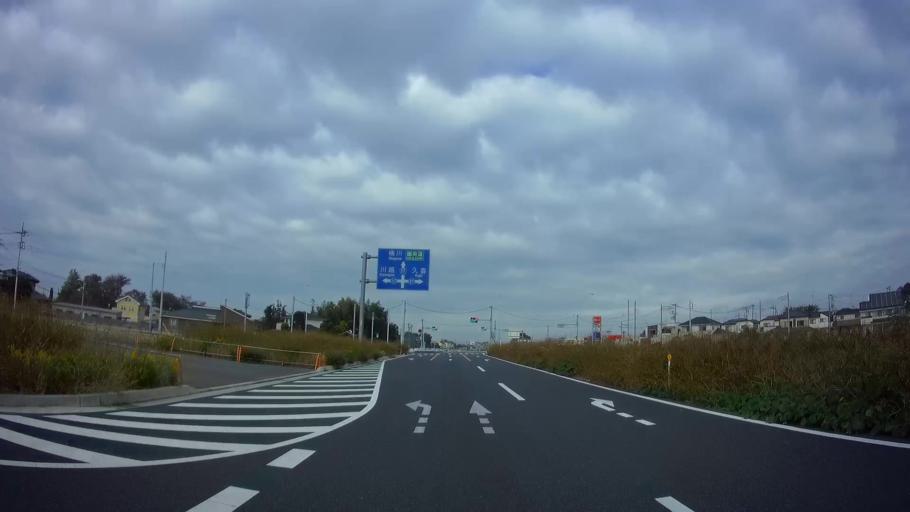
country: JP
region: Saitama
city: Okegawa
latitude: 35.9613
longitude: 139.5598
